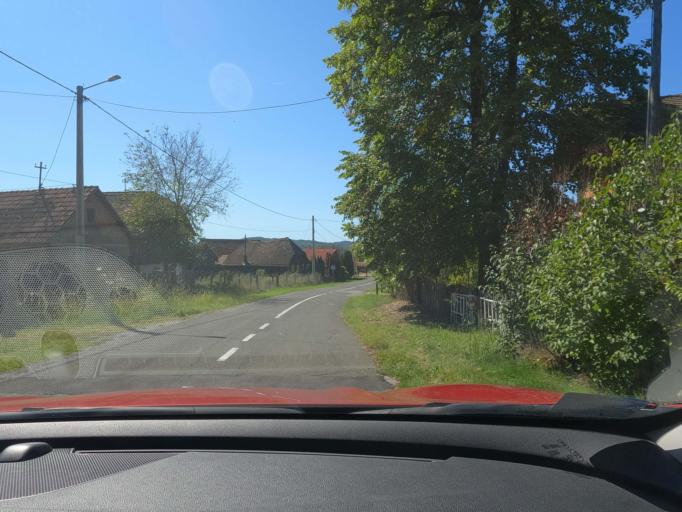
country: HR
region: Sisacko-Moslavacka
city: Petrinja
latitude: 45.3332
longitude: 16.2431
